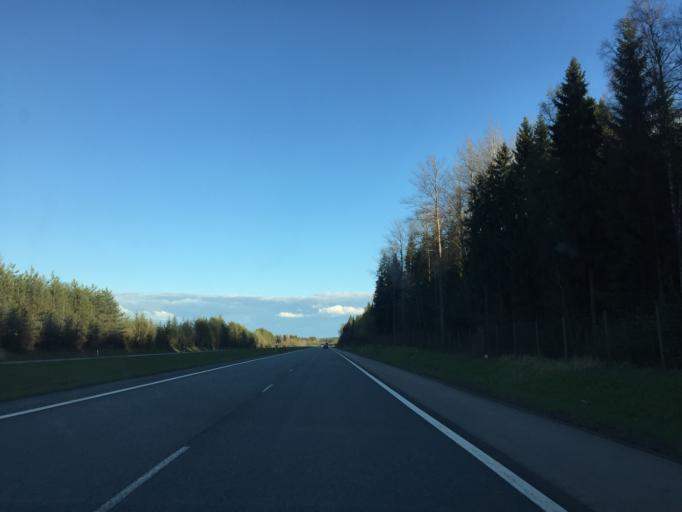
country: FI
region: Haeme
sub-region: Haemeenlinna
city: Tervakoski
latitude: 60.7903
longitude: 24.6961
